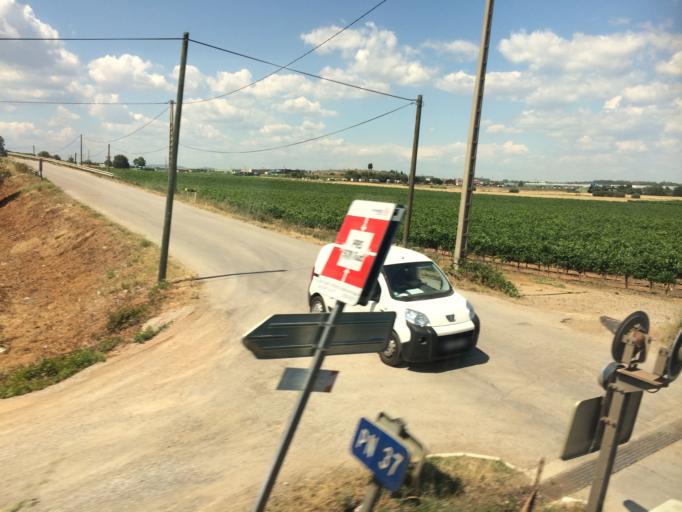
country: FR
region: Languedoc-Roussillon
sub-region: Departement de l'Herault
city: Saint-Aunes
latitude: 43.6371
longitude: 3.9742
